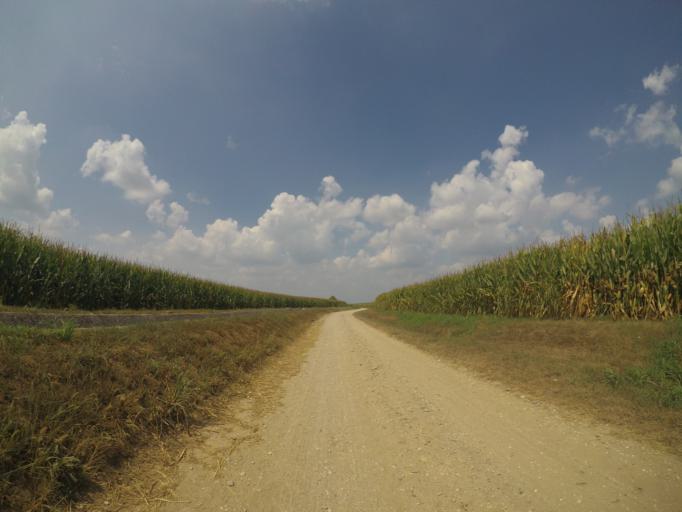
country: IT
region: Friuli Venezia Giulia
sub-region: Provincia di Udine
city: Bertiolo
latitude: 45.9472
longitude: 13.0430
